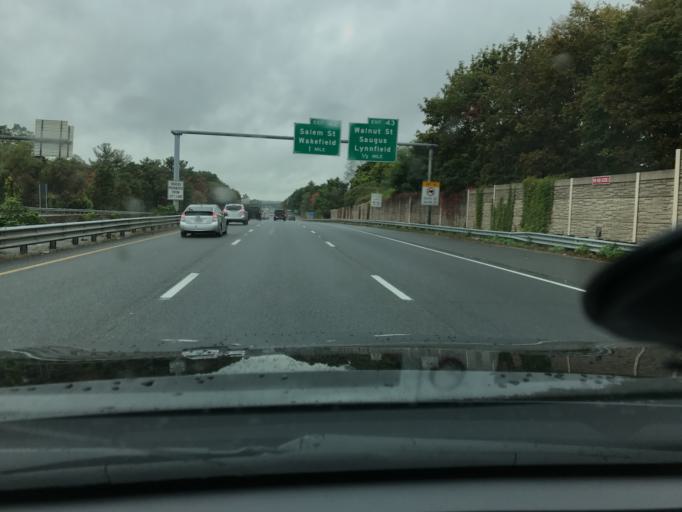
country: US
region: Massachusetts
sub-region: Essex County
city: Lynnfield
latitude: 42.5159
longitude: -71.0130
